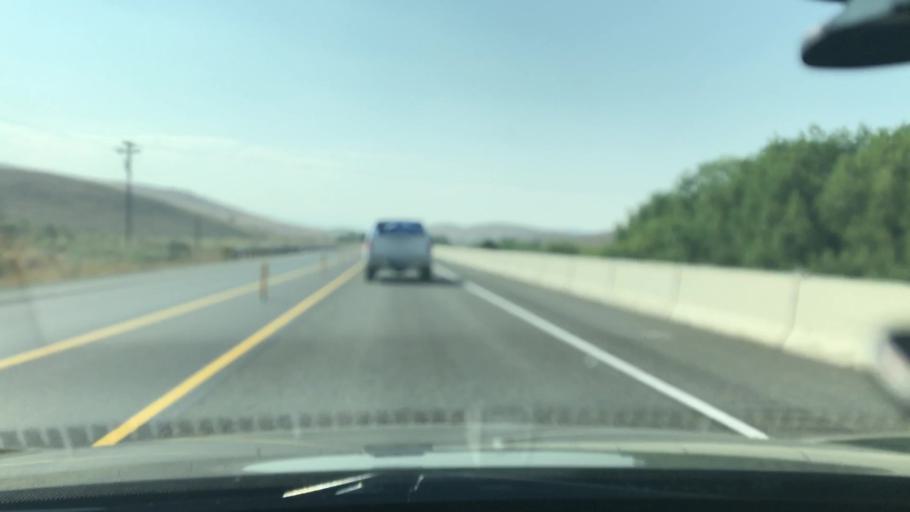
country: US
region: Oregon
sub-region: Baker County
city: Baker City
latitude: 44.6740
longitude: -117.6303
